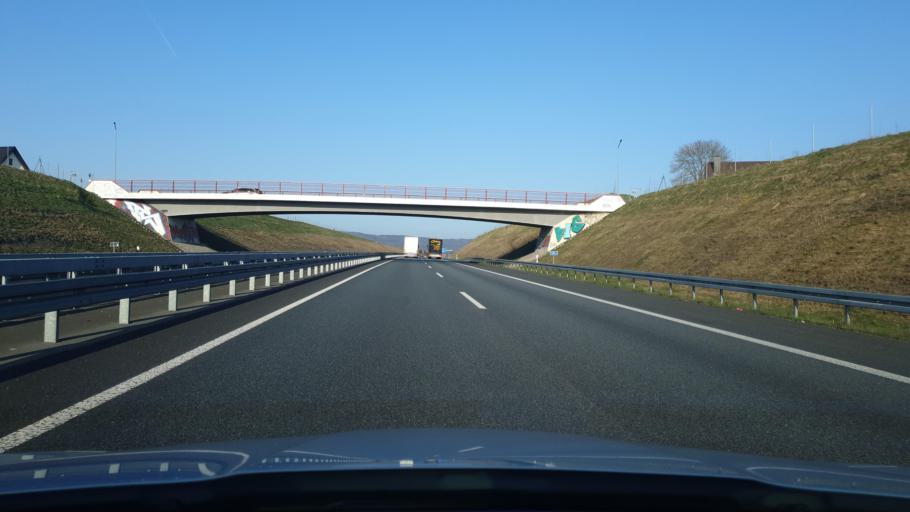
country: DE
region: North Rhine-Westphalia
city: Bad Oeynhausen
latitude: 52.2248
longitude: 8.7690
